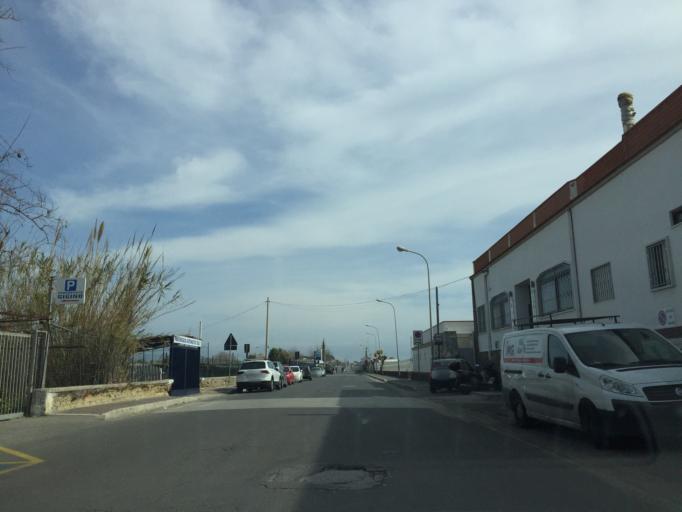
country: IT
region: Campania
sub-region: Provincia di Napoli
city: Bacoli
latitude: 40.7890
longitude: 14.0695
